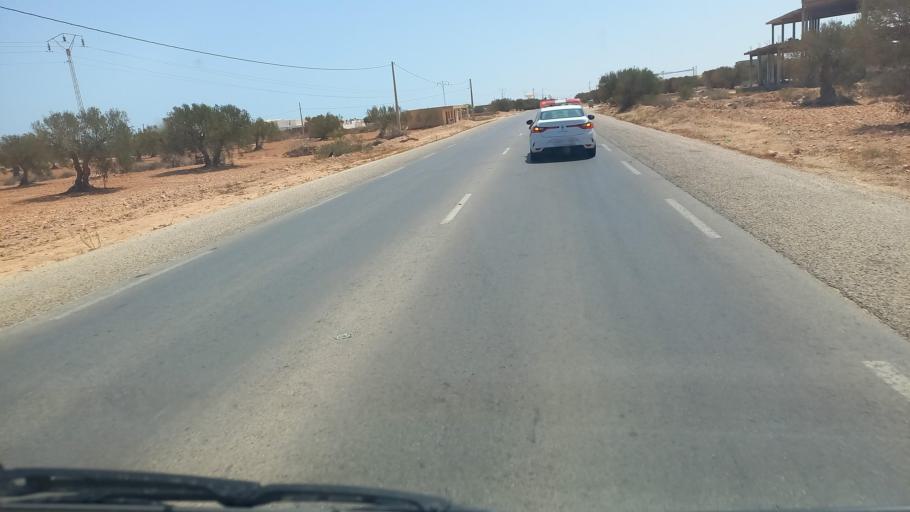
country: TN
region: Madanin
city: Zarzis
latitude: 33.5484
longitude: 11.0691
